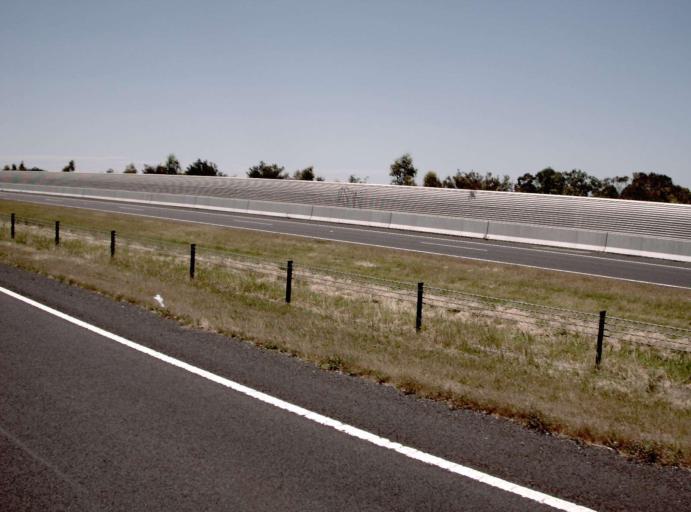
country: AU
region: Victoria
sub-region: Cardinia
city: Pakenham South
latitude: -38.0862
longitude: 145.5112
